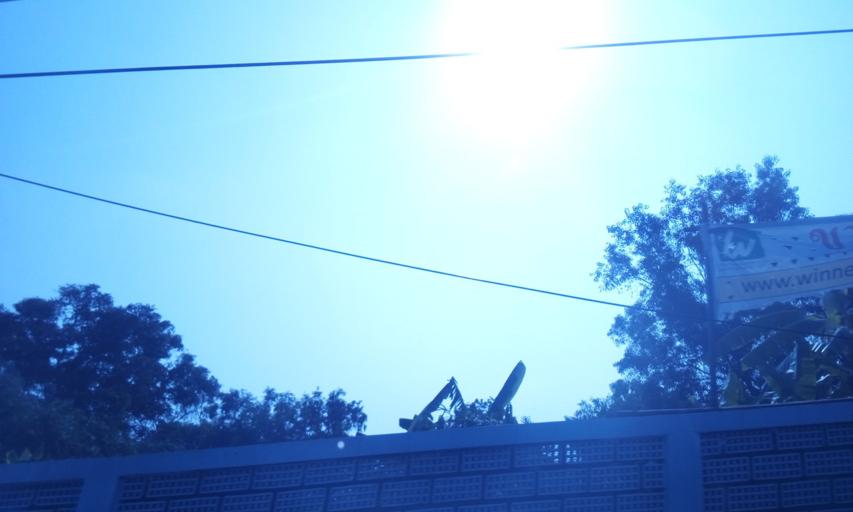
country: TH
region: Pathum Thani
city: Thanyaburi
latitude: 13.9759
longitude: 100.7061
